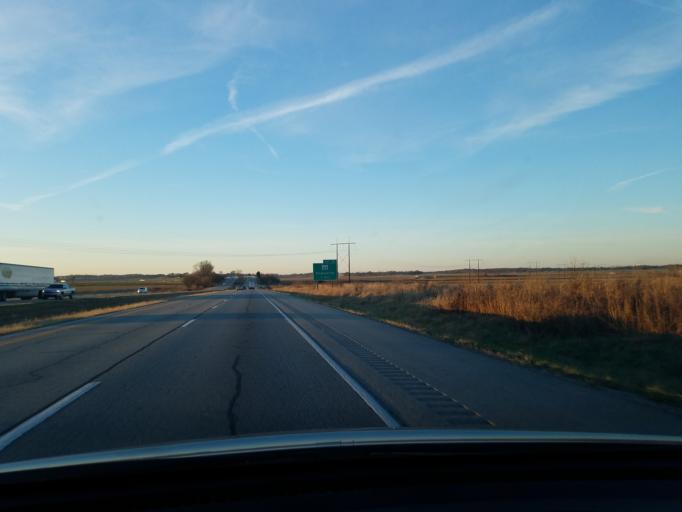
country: US
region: Indiana
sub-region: Posey County
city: Poseyville
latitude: 38.1759
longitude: -87.7578
